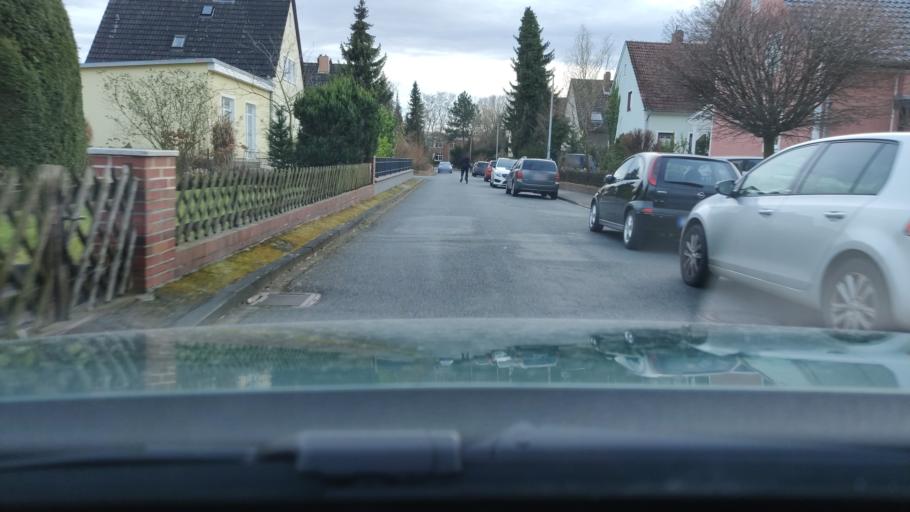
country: DE
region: Lower Saxony
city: Ilsede
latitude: 52.2669
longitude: 10.2280
